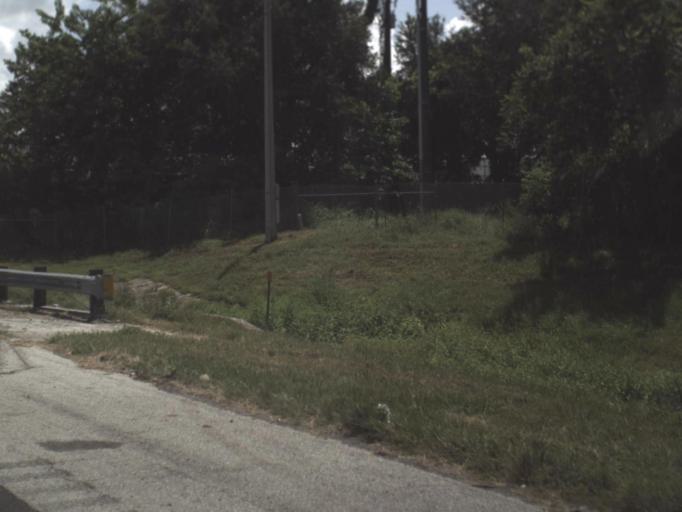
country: US
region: Florida
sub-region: Hillsborough County
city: Mango
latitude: 28.0043
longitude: -82.3111
